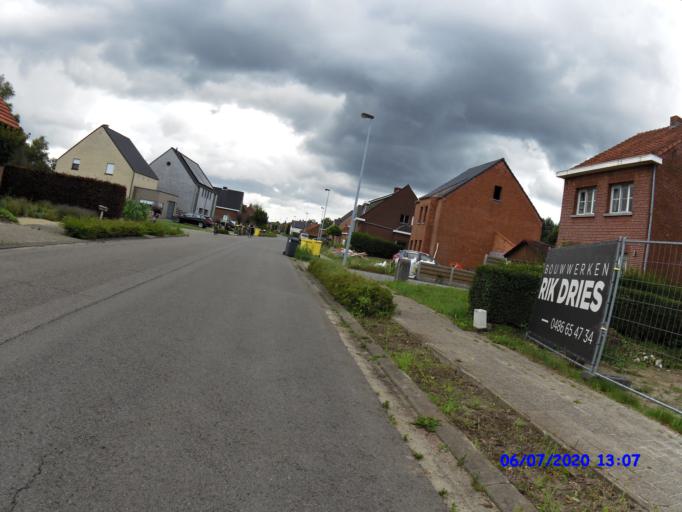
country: BE
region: Flanders
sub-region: Provincie Antwerpen
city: Dessel
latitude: 51.2385
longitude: 5.1330
